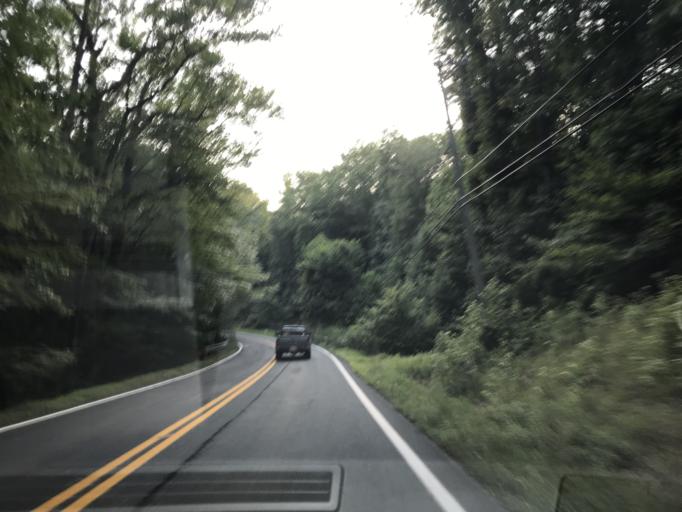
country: US
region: Maryland
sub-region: Cecil County
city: Charlestown
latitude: 39.5001
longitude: -75.9649
